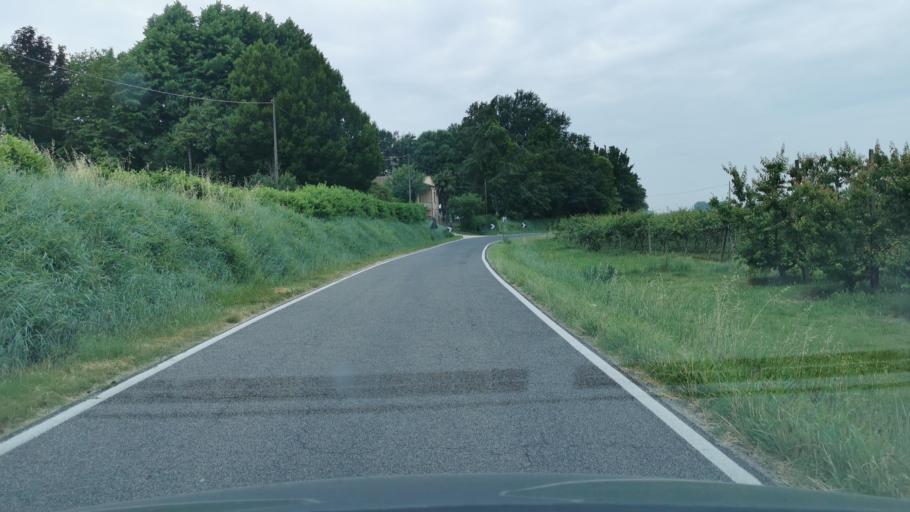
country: IT
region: Emilia-Romagna
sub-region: Provincia di Ravenna
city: Russi
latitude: 44.3881
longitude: 12.0077
